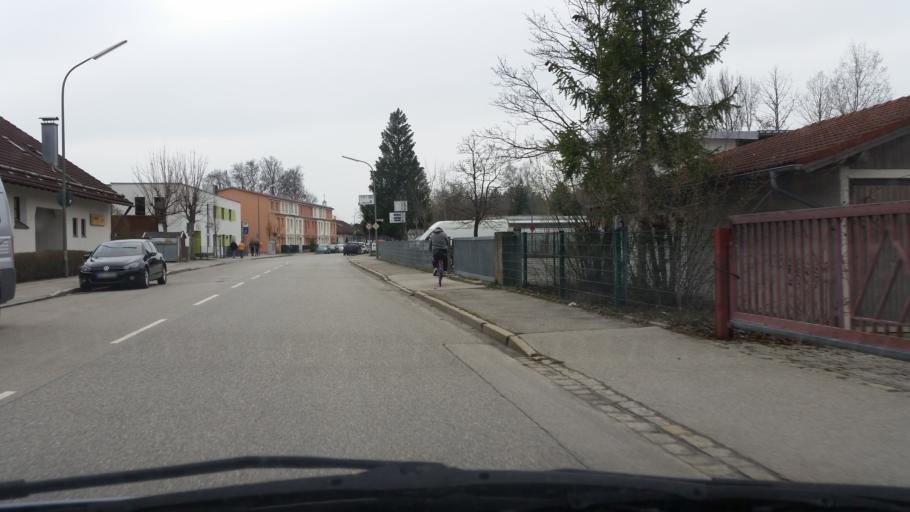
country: DE
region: Bavaria
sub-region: Upper Bavaria
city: Geretsried
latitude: 47.8512
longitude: 11.4883
